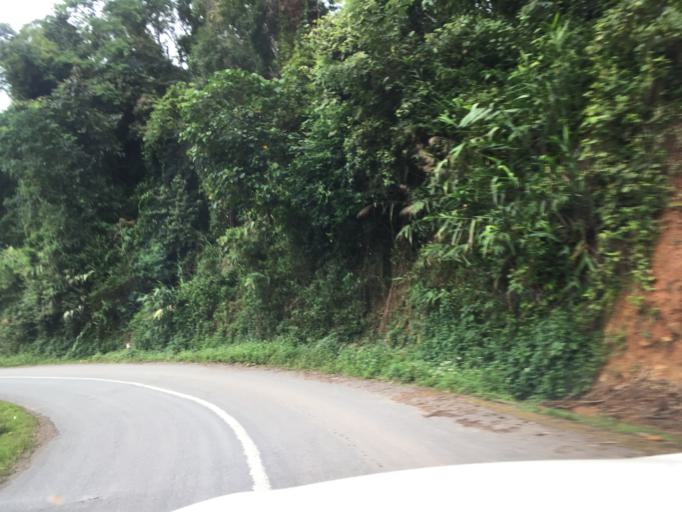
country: LA
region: Phongsali
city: Phongsali
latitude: 21.3365
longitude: 102.0485
